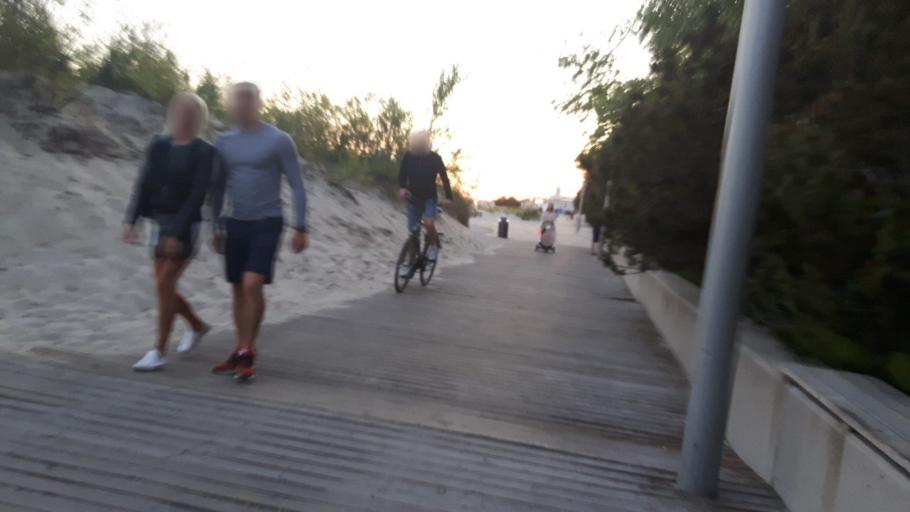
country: EE
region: Paernumaa
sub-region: Paernu linn
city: Parnu
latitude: 58.3727
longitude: 24.5042
